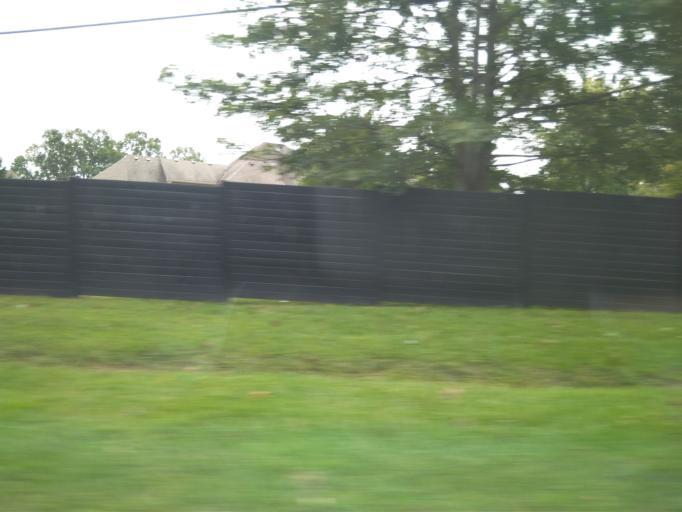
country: US
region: Kentucky
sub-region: Jefferson County
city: Anchorage
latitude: 38.2620
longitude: -85.4904
